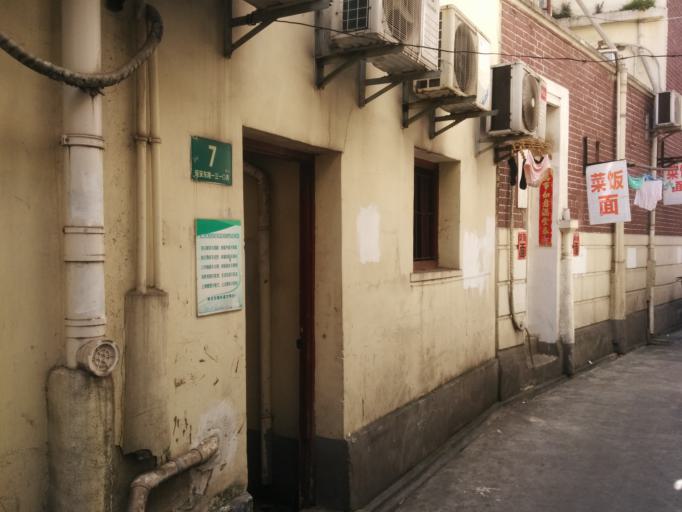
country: CN
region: Shanghai Shi
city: Shanghai
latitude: 31.2274
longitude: 121.4665
